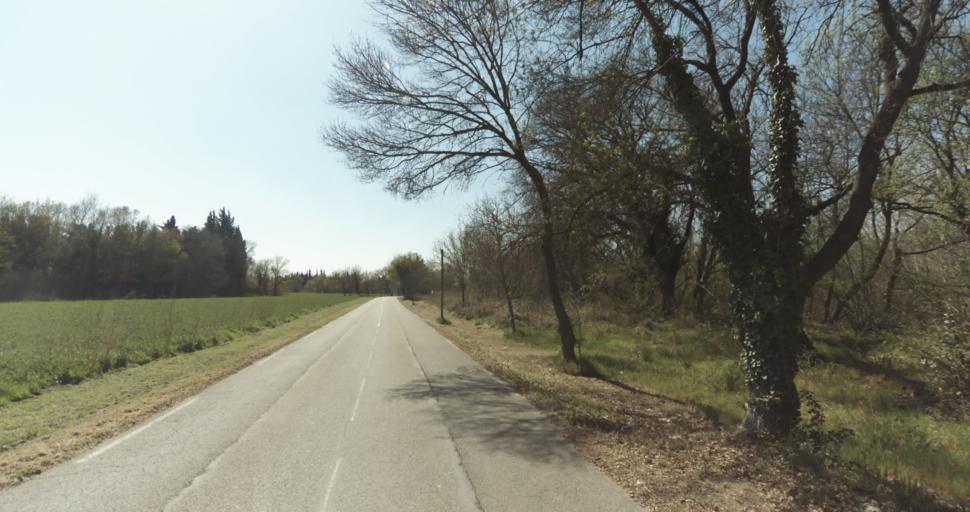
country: FR
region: Provence-Alpes-Cote d'Azur
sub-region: Departement des Bouches-du-Rhone
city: Pelissanne
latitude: 43.6270
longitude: 5.1370
